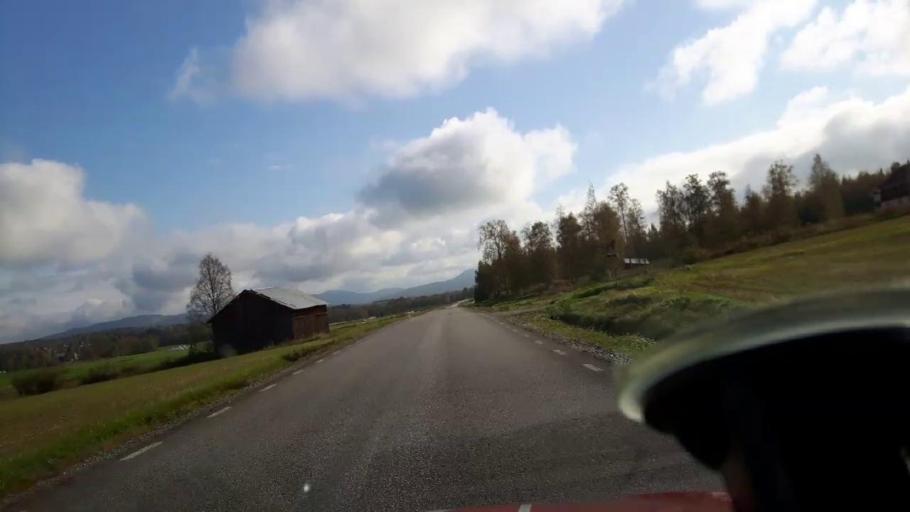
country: SE
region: Gaevleborg
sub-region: Ljusdals Kommun
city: Ljusdal
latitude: 61.7621
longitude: 16.0777
